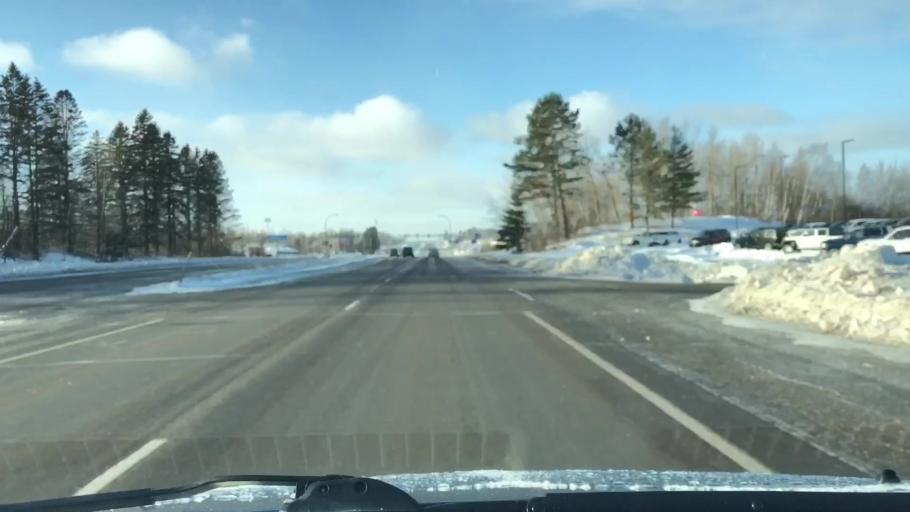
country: US
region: Minnesota
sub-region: Saint Louis County
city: Hermantown
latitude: 46.8177
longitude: -92.1793
